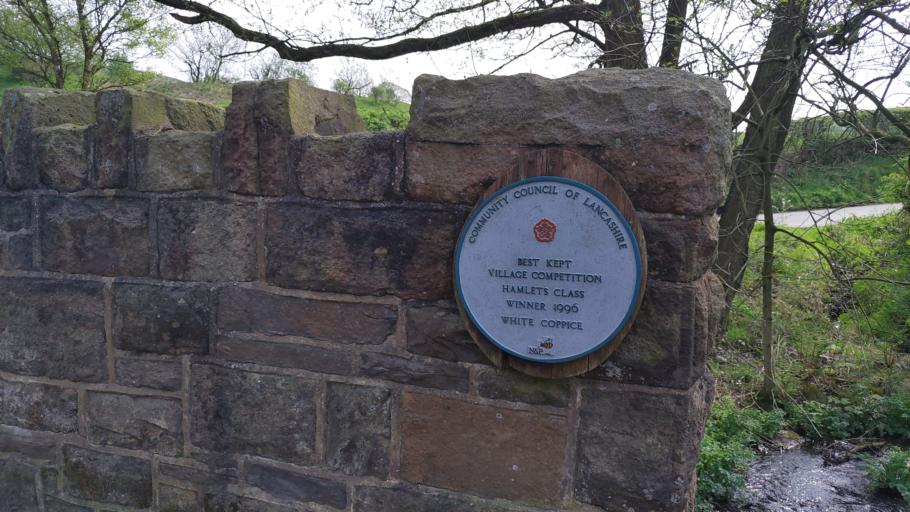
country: GB
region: England
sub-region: Lancashire
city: Chorley
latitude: 53.6669
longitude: -2.5850
